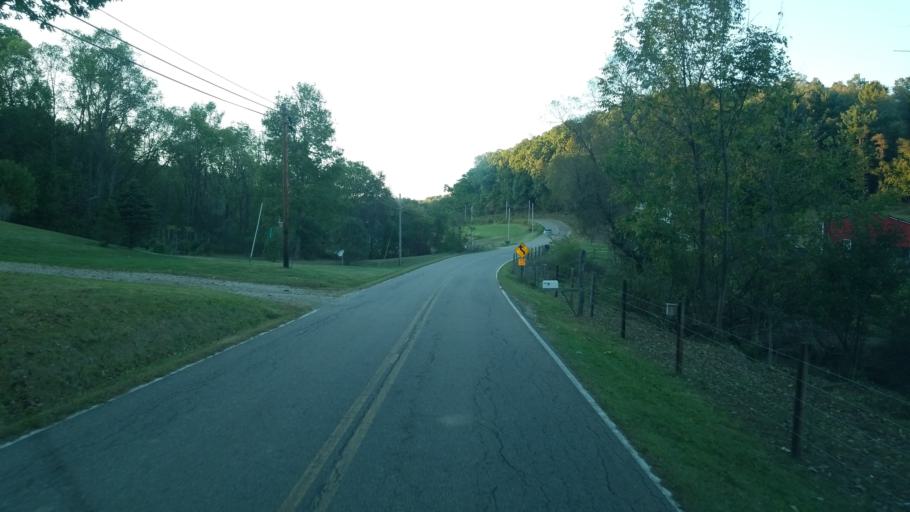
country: US
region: Ohio
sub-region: Licking County
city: Utica
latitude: 40.1651
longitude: -82.3850
